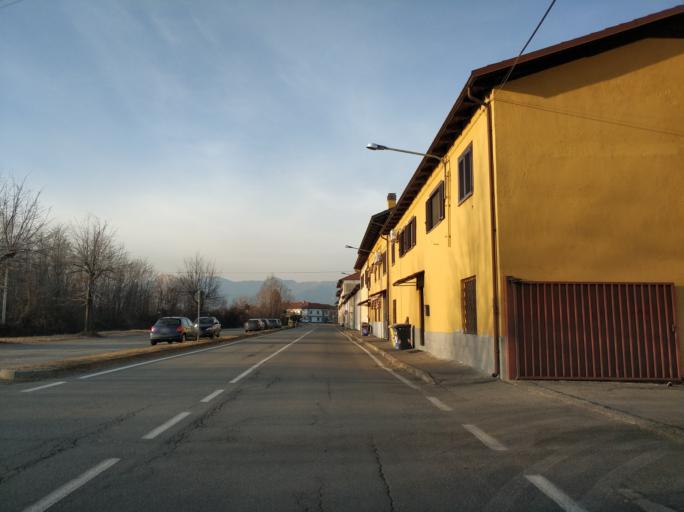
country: IT
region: Piedmont
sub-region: Provincia di Torino
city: San Francesco al Campo
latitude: 45.2206
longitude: 7.6470
